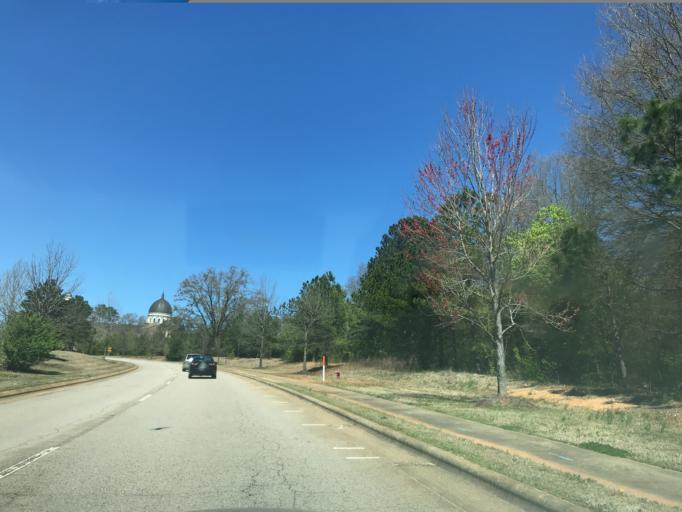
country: US
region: North Carolina
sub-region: Wake County
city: West Raleigh
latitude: 35.7739
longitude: -78.6686
